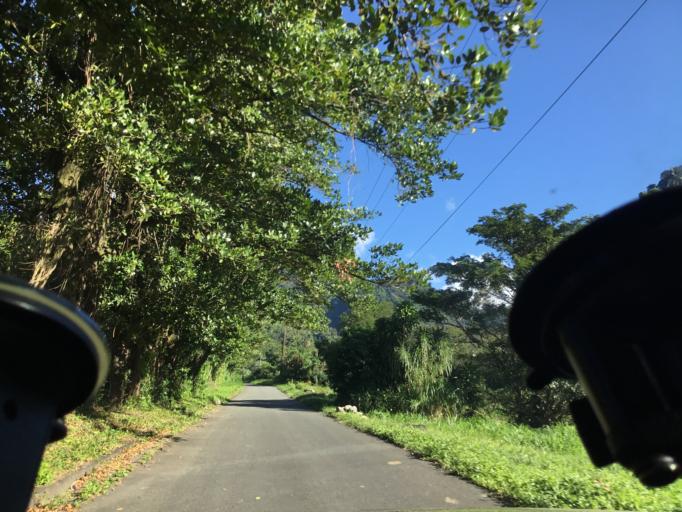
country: VC
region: Saint David
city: Chateaubelair
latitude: 13.3077
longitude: -61.2327
